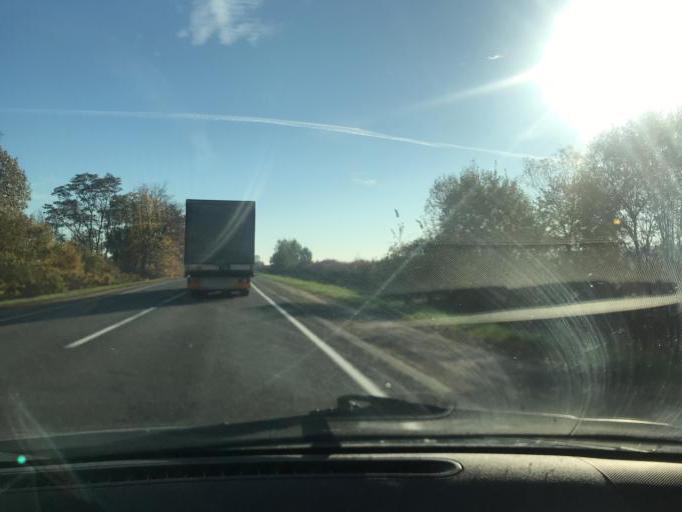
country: BY
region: Brest
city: Ivanava
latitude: 52.1474
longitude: 25.4356
